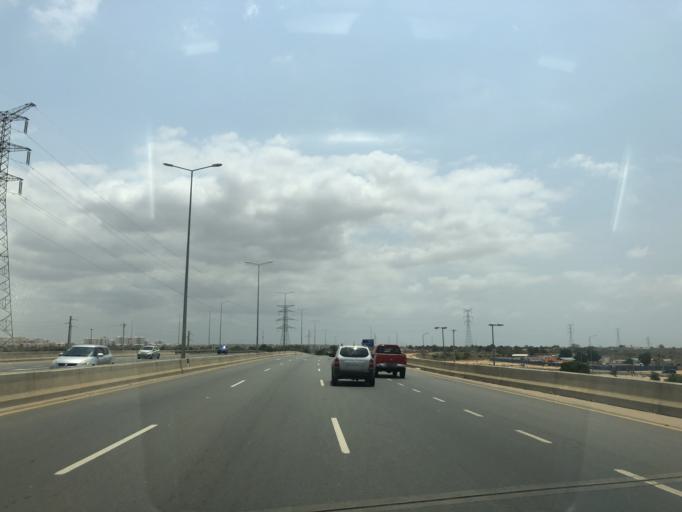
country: AO
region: Luanda
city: Luanda
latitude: -8.9729
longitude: 13.2541
